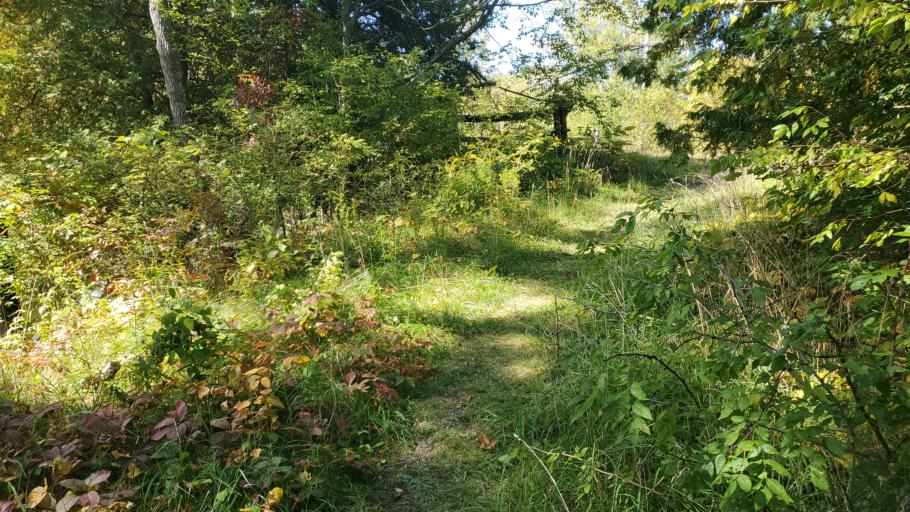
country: CA
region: Ontario
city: Belleville
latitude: 44.5480
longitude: -77.3270
